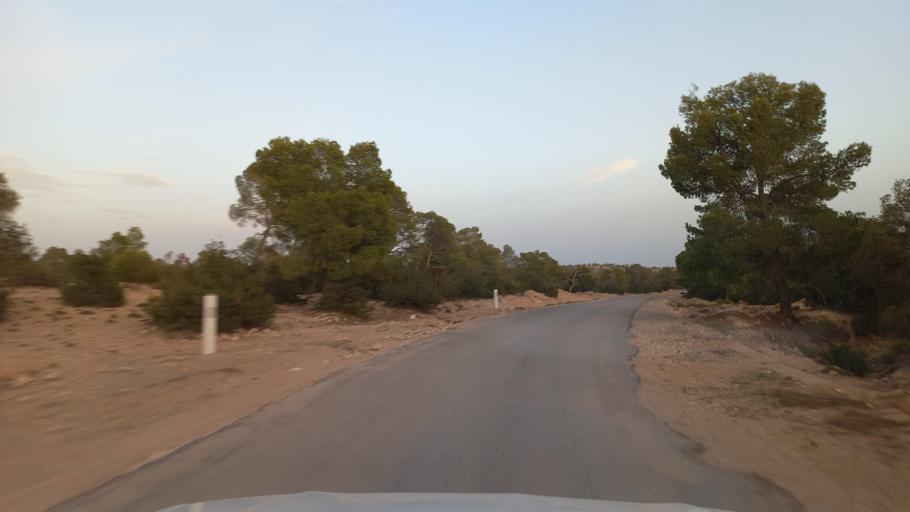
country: TN
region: Al Qasrayn
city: Sbiba
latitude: 35.4129
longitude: 8.9427
